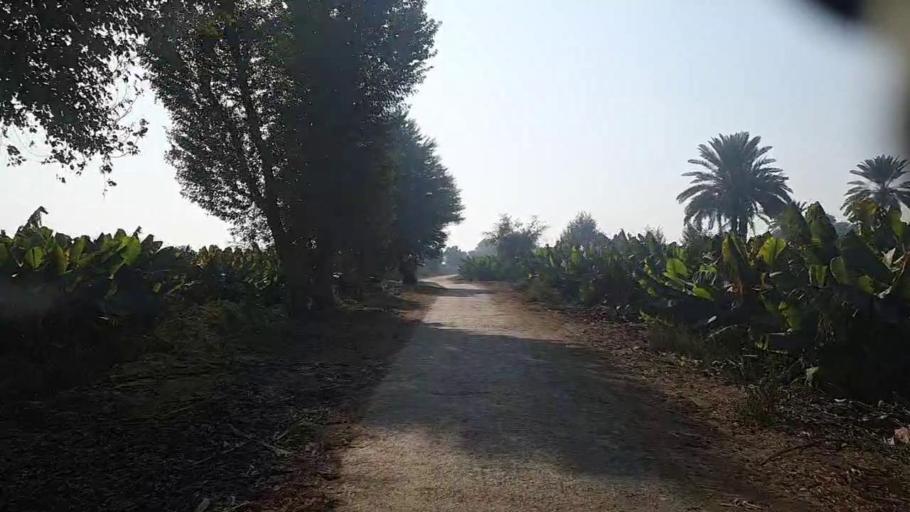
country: PK
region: Sindh
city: Kandiari
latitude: 27.0180
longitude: 68.5017
